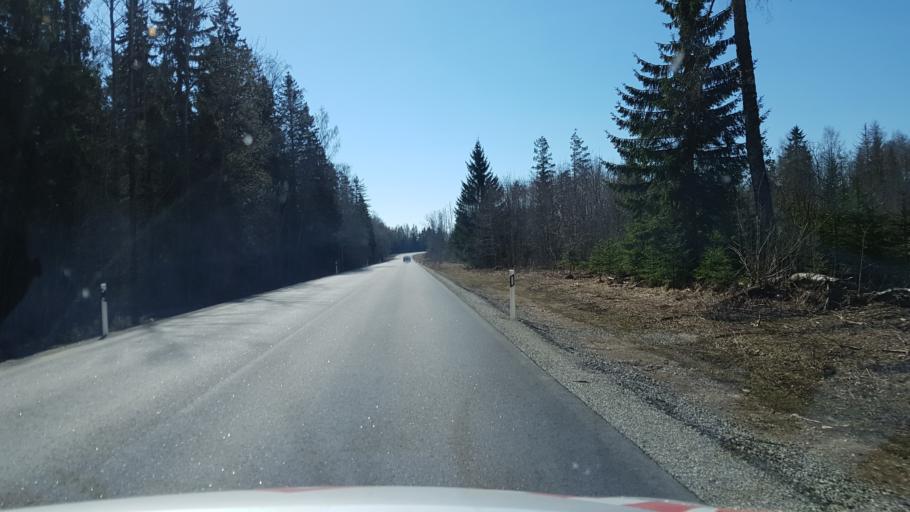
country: EE
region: Laeaene-Virumaa
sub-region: Vinni vald
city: Vinni
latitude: 59.1232
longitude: 26.6169
